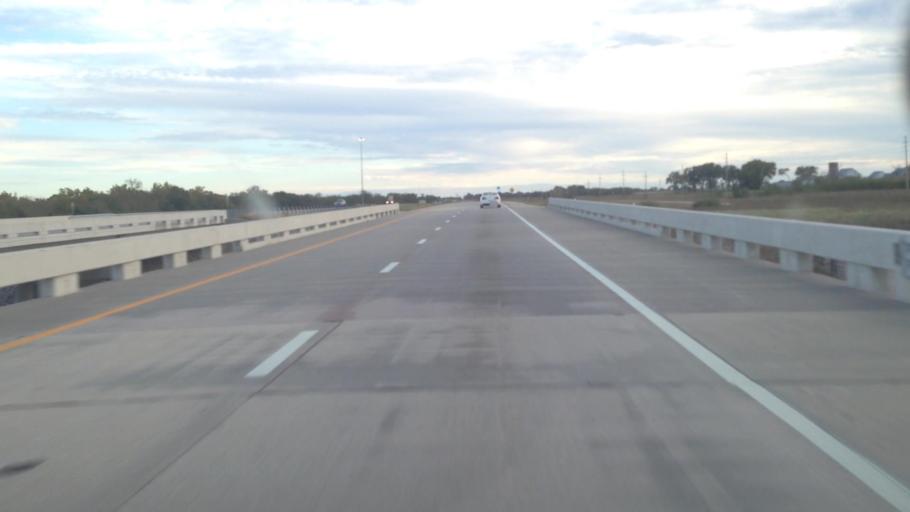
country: US
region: Kansas
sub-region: Franklin County
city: Ottawa
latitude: 38.7099
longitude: -95.2686
